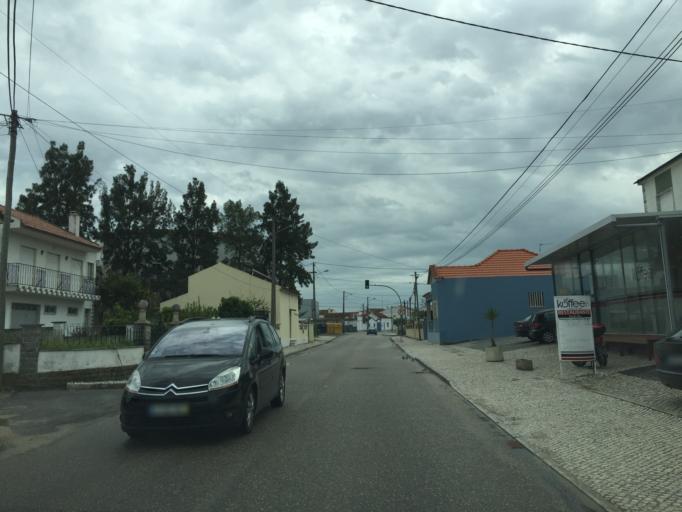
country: PT
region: Lisbon
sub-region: Azambuja
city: Aveiras de Cima
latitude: 39.1428
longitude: -8.9007
